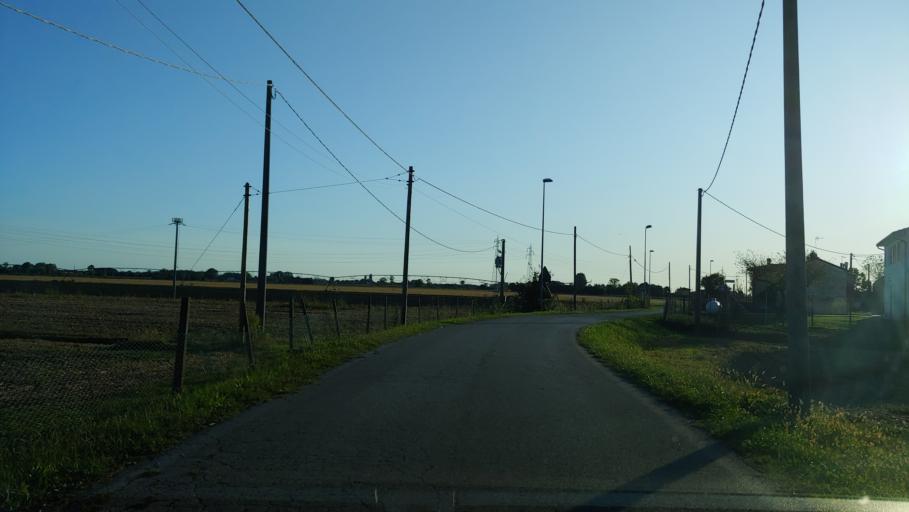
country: IT
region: Veneto
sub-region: Provincia di Rovigo
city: Adria
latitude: 45.0760
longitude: 11.9997
